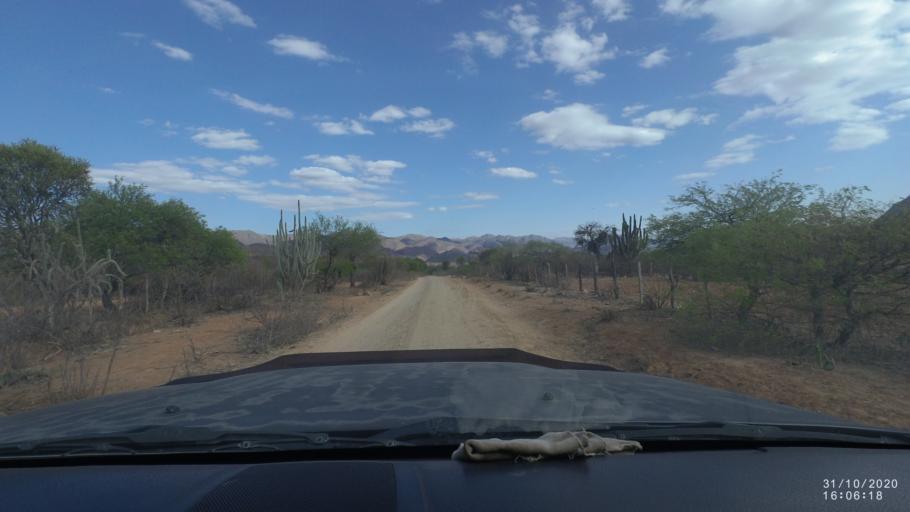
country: BO
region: Chuquisaca
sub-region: Provincia Zudanez
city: Mojocoya
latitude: -18.3724
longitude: -64.6479
